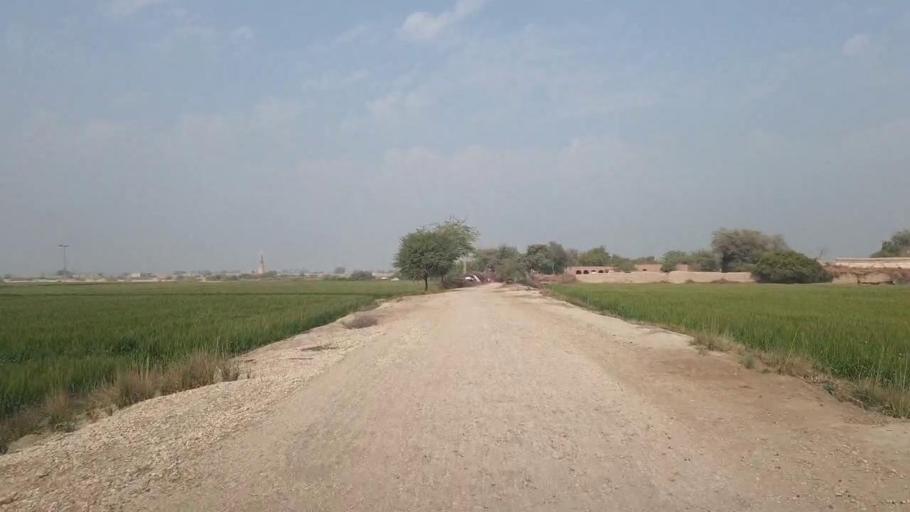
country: PK
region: Sindh
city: Hala
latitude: 25.7842
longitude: 68.4297
